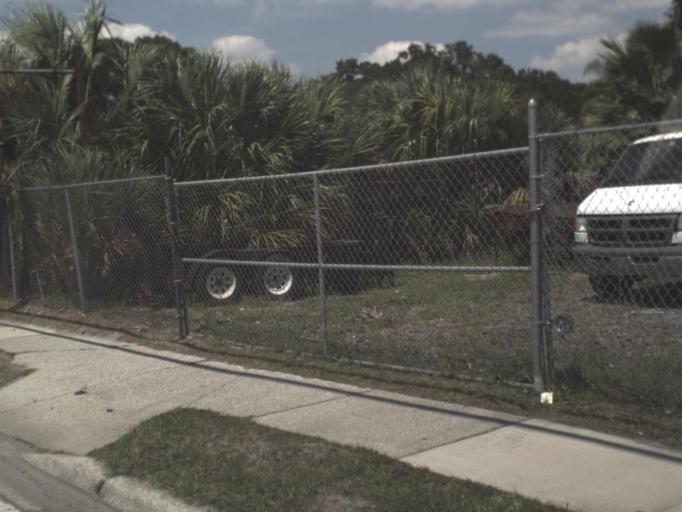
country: US
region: Florida
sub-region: Hillsborough County
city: Palm River-Clair Mel
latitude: 27.9279
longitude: -82.4018
